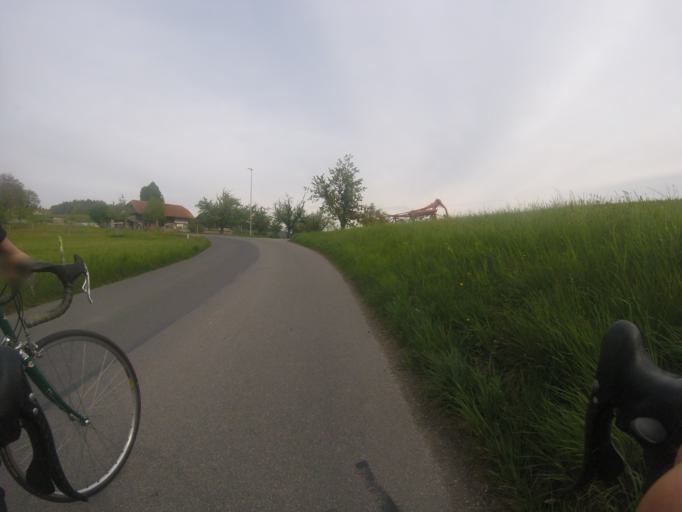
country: CH
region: Bern
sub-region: Bern-Mittelland District
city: Niederwichtrach
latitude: 46.8409
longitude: 7.5908
